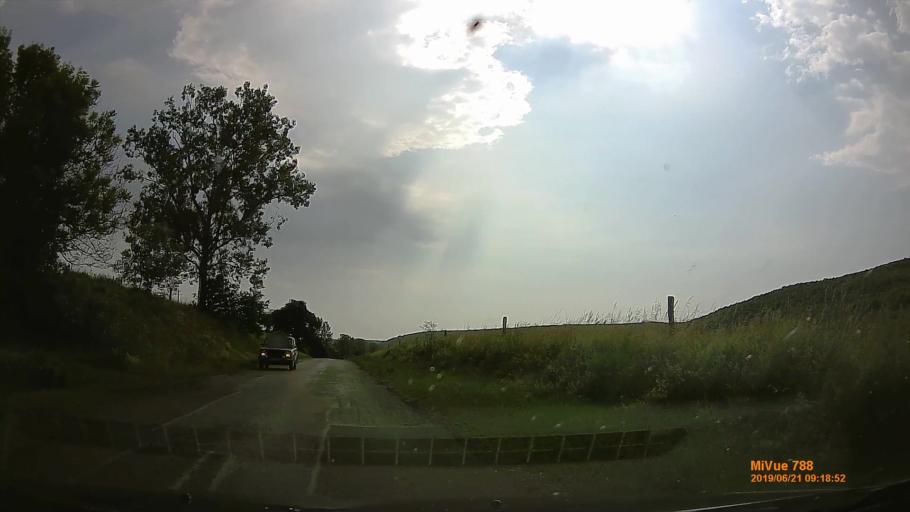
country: HU
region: Somogy
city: Kaposvar
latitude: 46.2312
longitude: 17.8549
